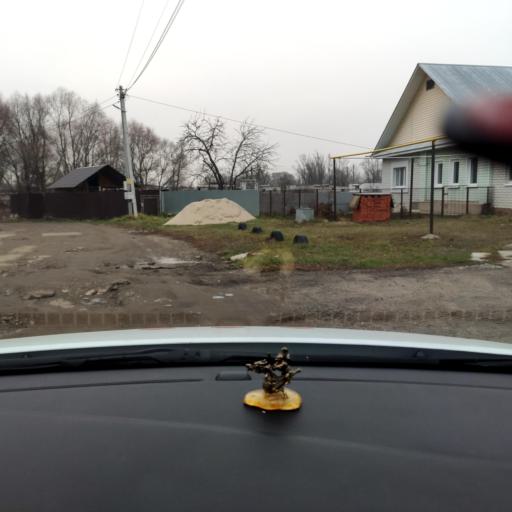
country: RU
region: Tatarstan
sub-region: Gorod Kazan'
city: Kazan
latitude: 55.8468
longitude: 49.1573
